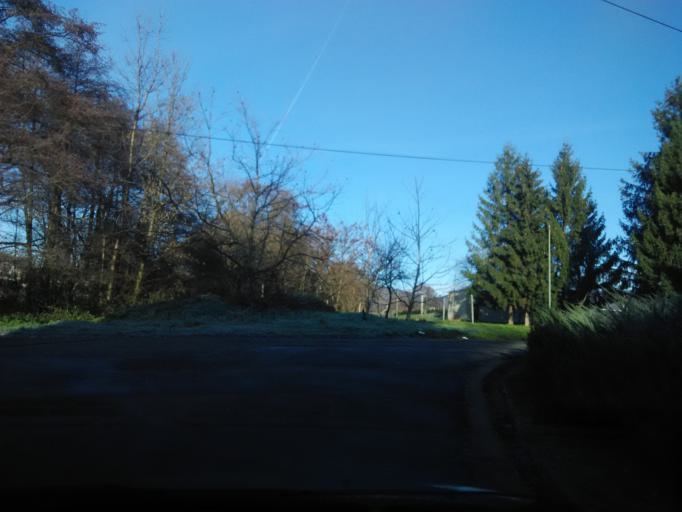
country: SK
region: Nitriansky
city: Tlmace
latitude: 48.3594
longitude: 18.5290
